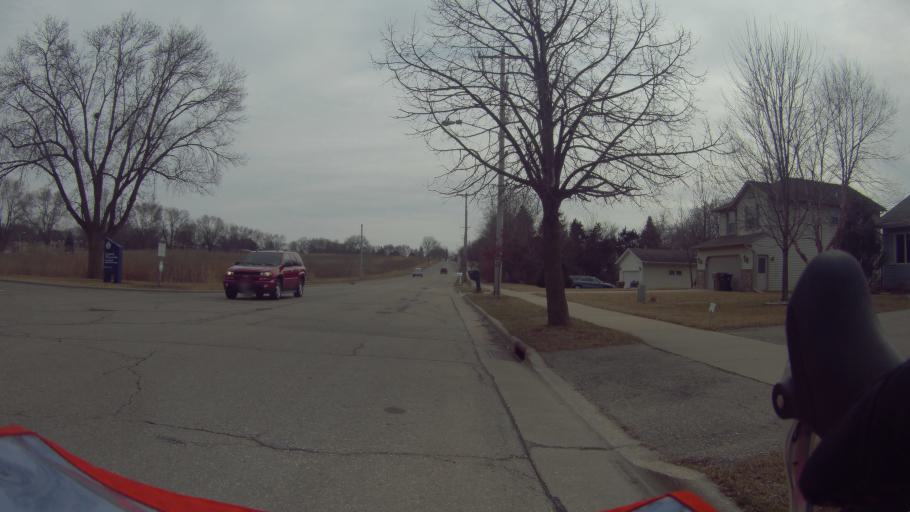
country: US
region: Wisconsin
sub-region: Dane County
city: Maple Bluff
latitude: 43.1392
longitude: -89.3978
